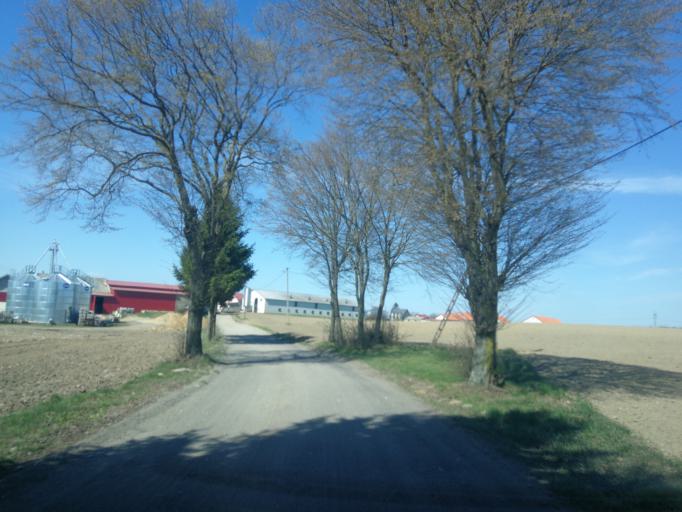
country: PL
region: Warmian-Masurian Voivodeship
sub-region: Powiat dzialdowski
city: Rybno
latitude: 53.4378
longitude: 19.9584
